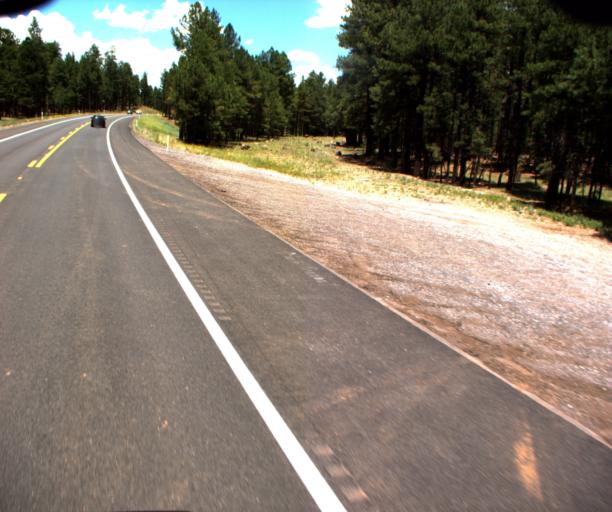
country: US
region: Arizona
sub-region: Coconino County
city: Flagstaff
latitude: 35.2556
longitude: -111.7020
